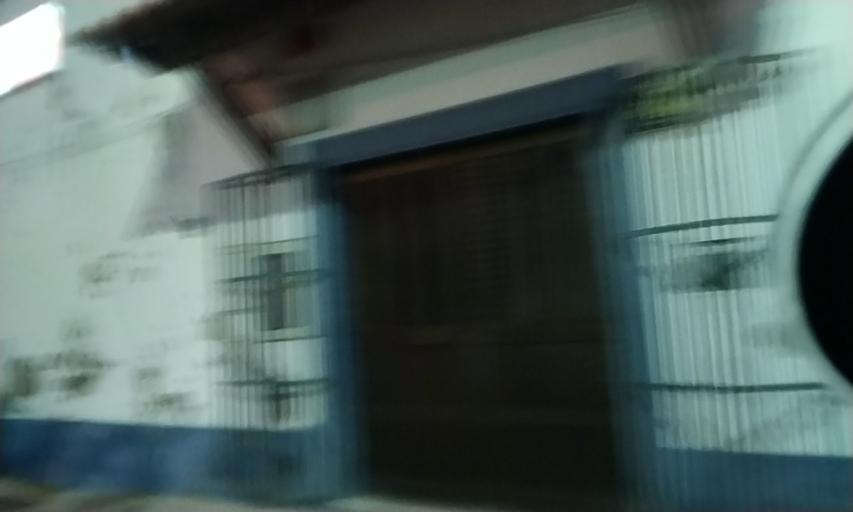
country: PT
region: Setubal
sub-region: Setubal
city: Setubal
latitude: 38.5302
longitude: -8.8927
